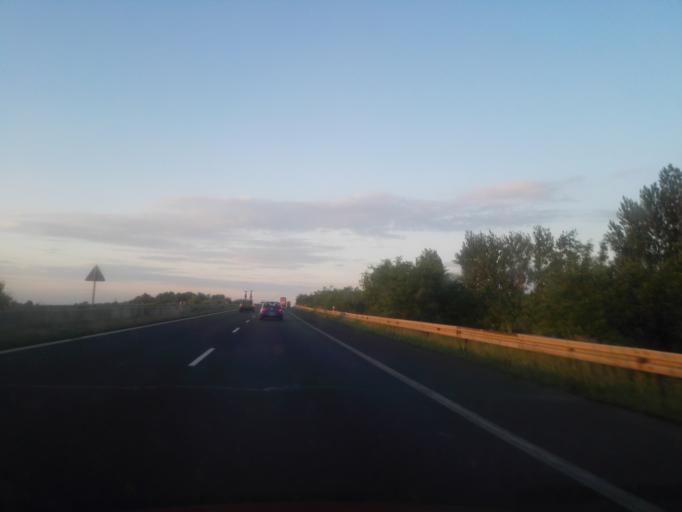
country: PL
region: Silesian Voivodeship
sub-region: Powiat czestochowski
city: Koscielec
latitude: 50.8877
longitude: 19.1749
